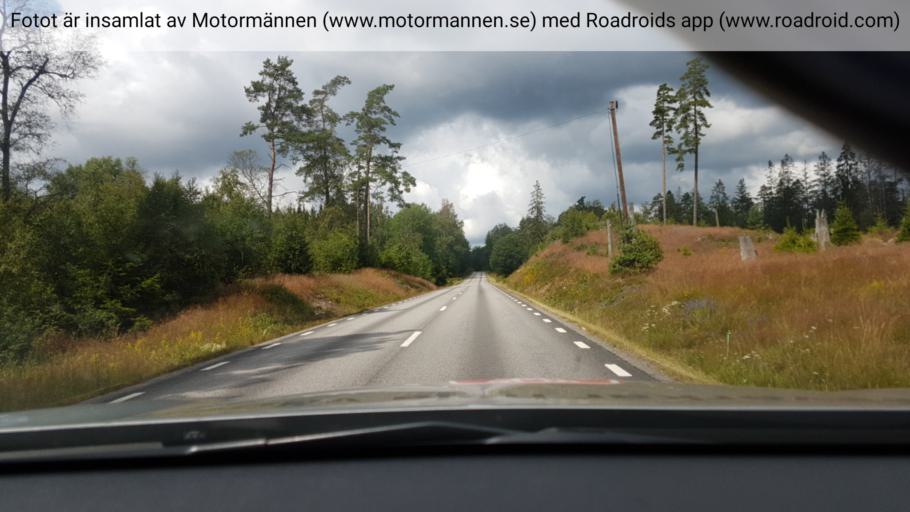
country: SE
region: Vaestra Goetaland
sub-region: Svenljunga Kommun
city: Svenljunga
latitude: 57.4722
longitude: 13.1663
